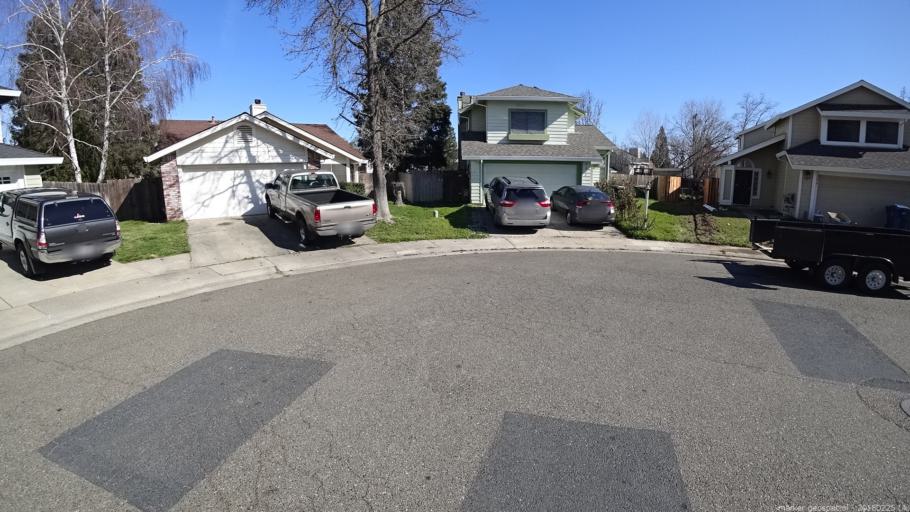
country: US
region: California
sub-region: Sacramento County
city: North Highlands
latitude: 38.7230
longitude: -121.3875
